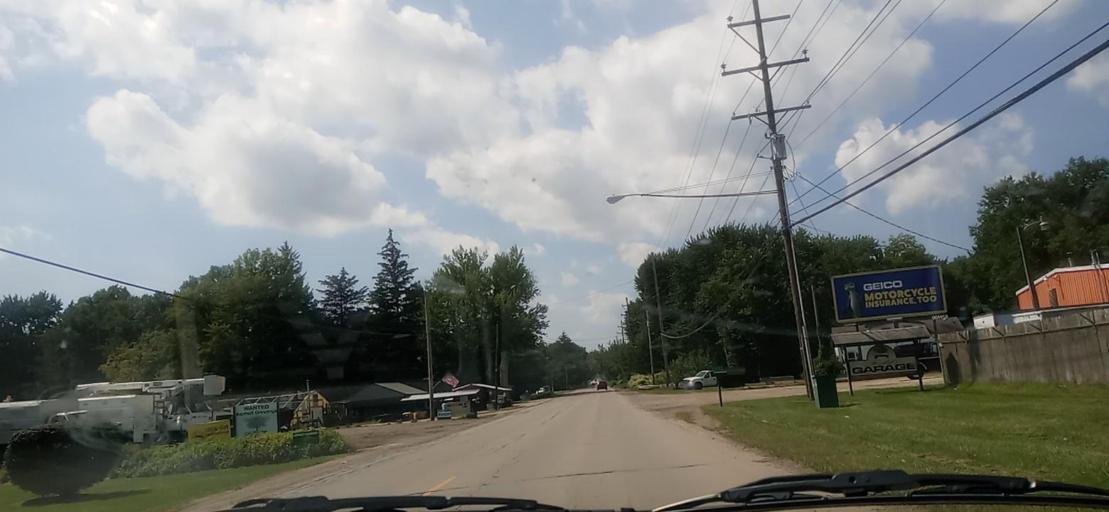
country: US
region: Ohio
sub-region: Summit County
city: Barberton
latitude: 41.0571
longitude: -81.6004
